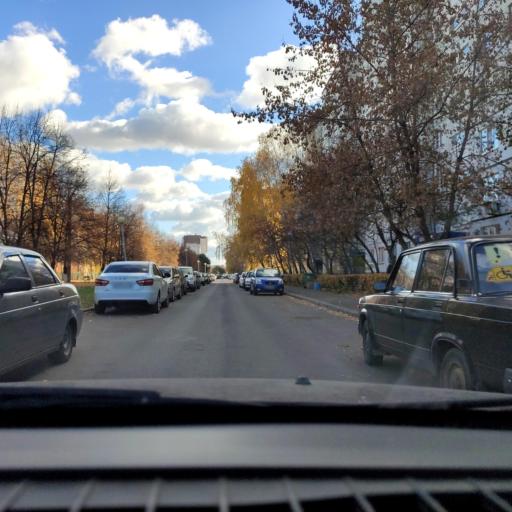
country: RU
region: Samara
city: Tol'yatti
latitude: 53.5245
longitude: 49.3124
